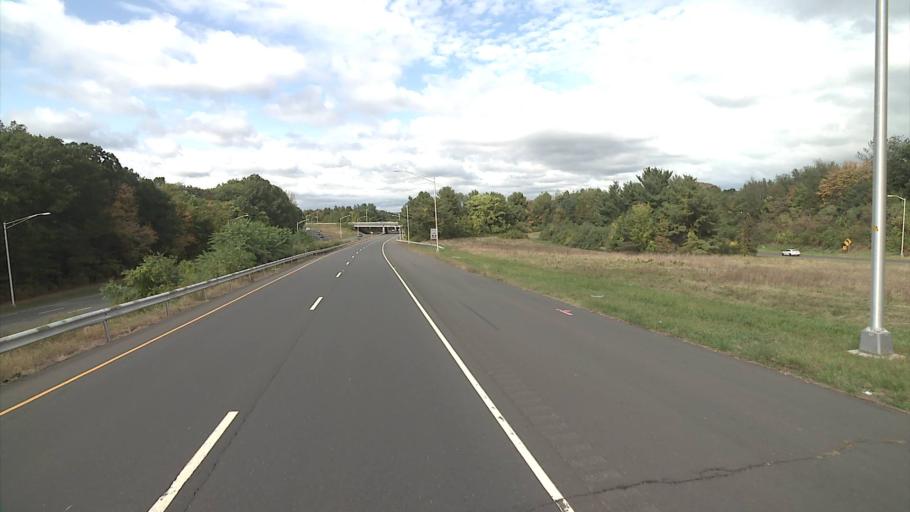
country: US
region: Connecticut
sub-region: New Haven County
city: Meriden
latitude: 41.5366
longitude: -72.7691
